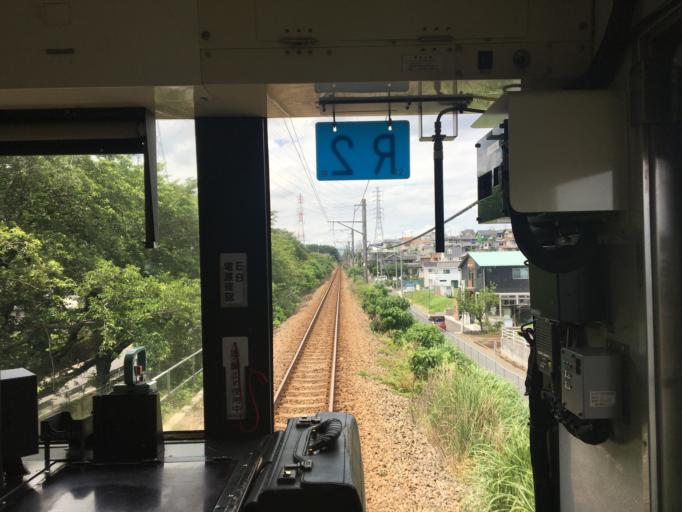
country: JP
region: Kanagawa
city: Zama
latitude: 35.5039
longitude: 139.3854
